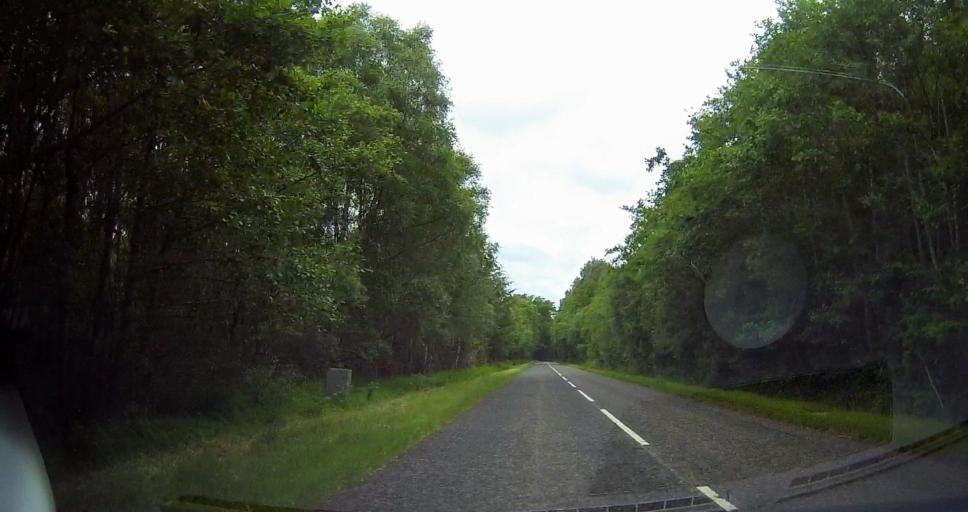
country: GB
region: Scotland
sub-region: Highland
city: Dornoch
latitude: 57.9588
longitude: -4.0711
